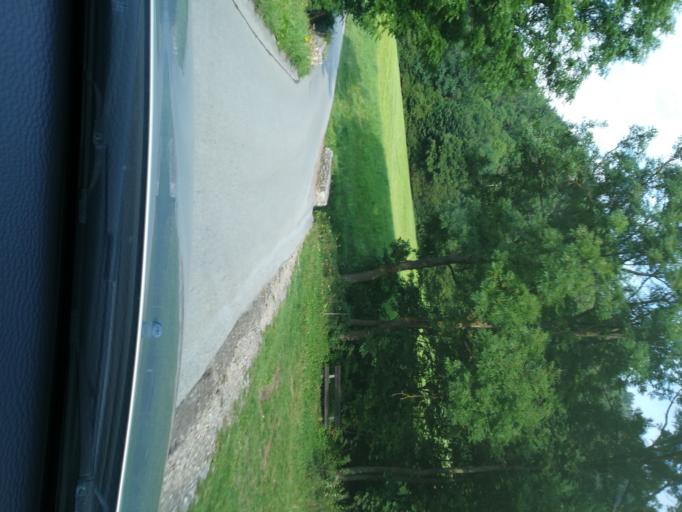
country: AT
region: Styria
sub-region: Politischer Bezirk Murtal
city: Sankt Georgen ob Judenburg
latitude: 47.2158
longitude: 14.4780
